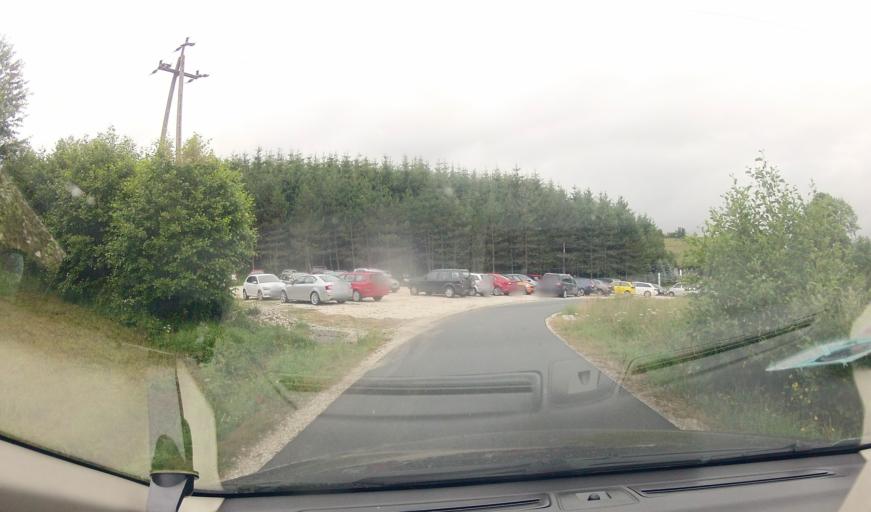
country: PL
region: Lower Silesian Voivodeship
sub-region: Powiat klodzki
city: Miedzylesie
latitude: 50.1225
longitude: 16.6593
